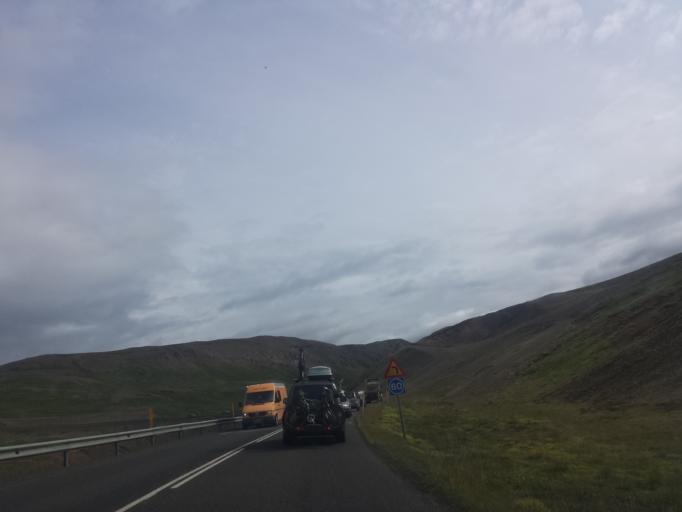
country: IS
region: Northeast
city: Akureyri
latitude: 65.8135
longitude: -18.0070
